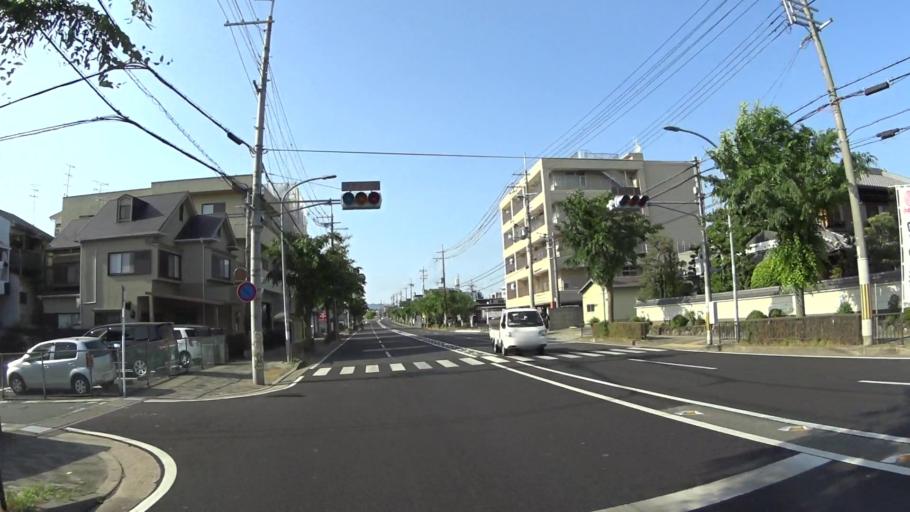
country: JP
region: Kyoto
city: Muko
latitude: 34.9364
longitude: 135.6913
